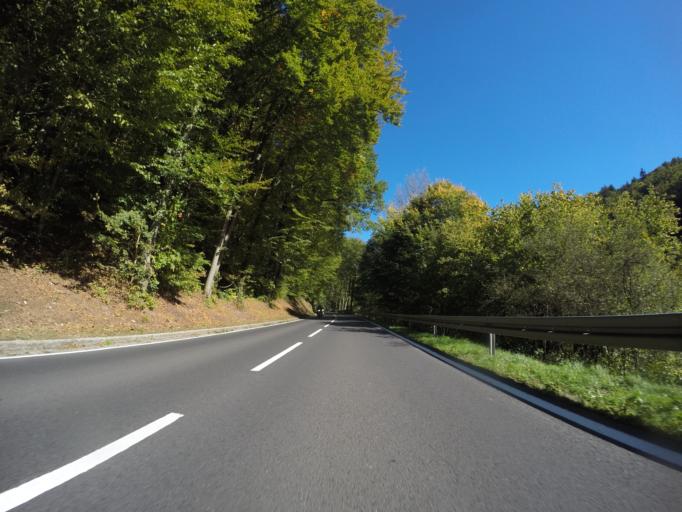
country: DE
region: Bavaria
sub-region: Upper Franconia
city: Gossweinstein
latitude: 49.7747
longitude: 11.3008
